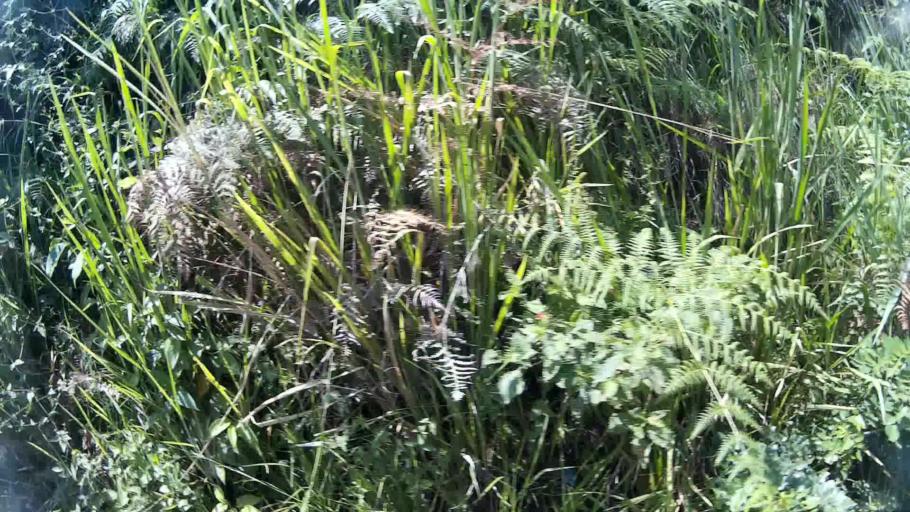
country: CO
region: Caldas
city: Belalcazar
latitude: 4.9460
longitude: -75.8370
